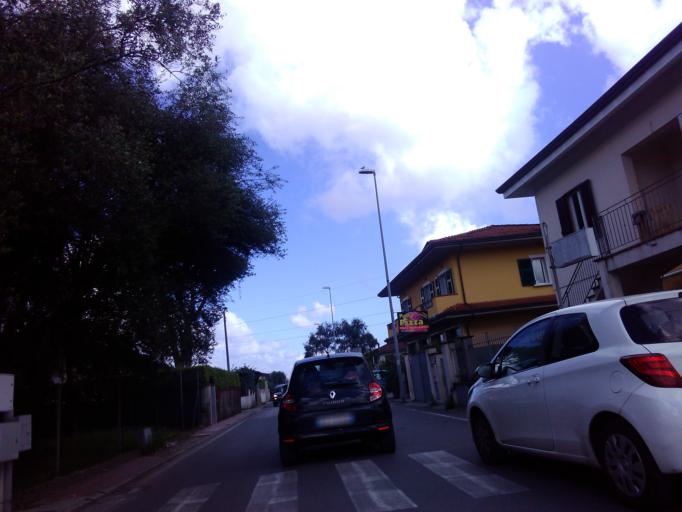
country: IT
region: Tuscany
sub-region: Provincia di Massa-Carrara
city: Massa
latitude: 44.0176
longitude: 10.1247
